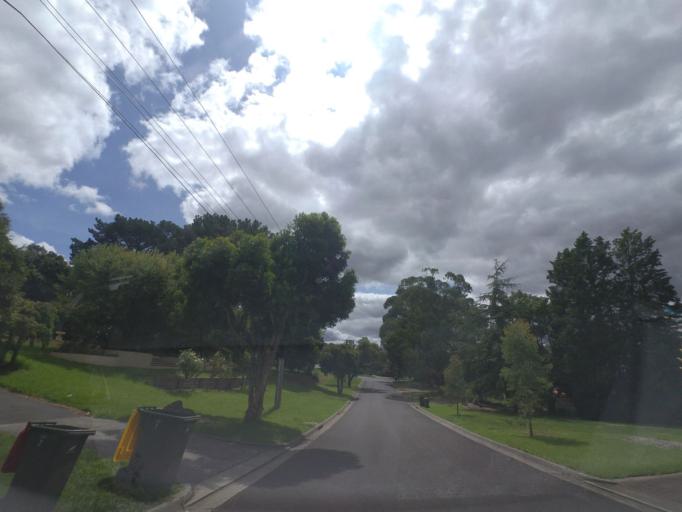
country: AU
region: Victoria
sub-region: Manningham
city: Park Orchards
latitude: -37.7878
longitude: 145.2306
